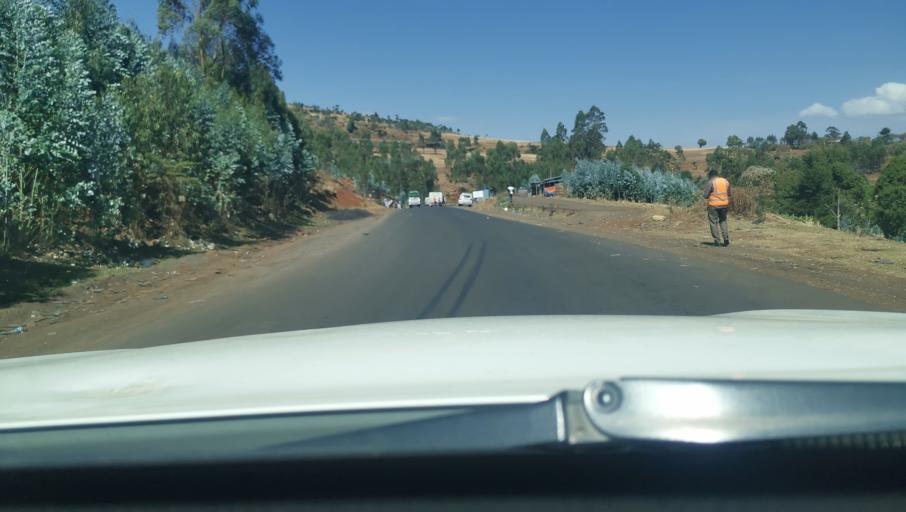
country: ET
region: Oromiya
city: Gedo
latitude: 9.0018
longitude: 37.4666
